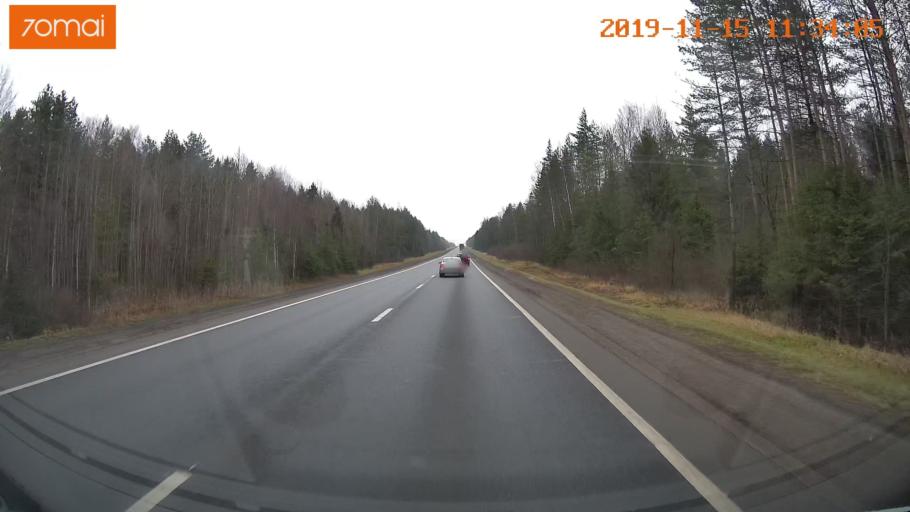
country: RU
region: Vologda
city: Molochnoye
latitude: 59.1918
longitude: 39.6048
